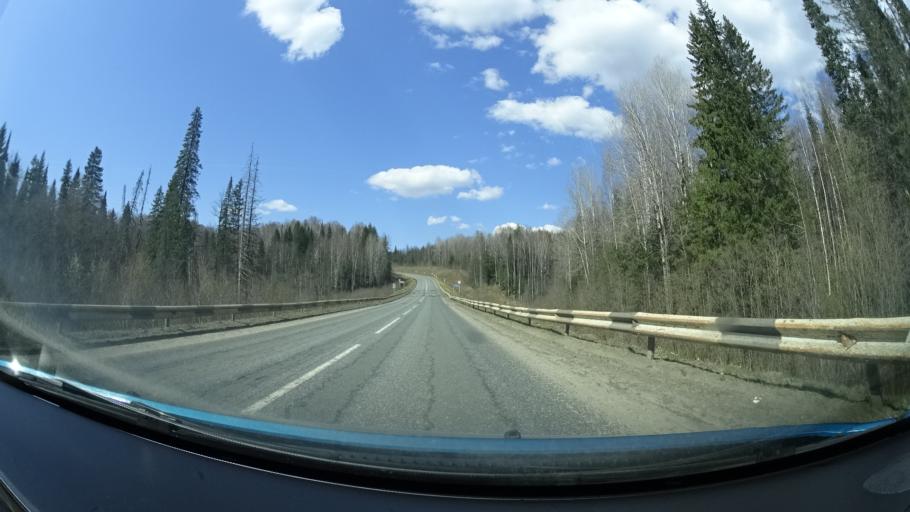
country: RU
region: Perm
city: Yugo-Kamskiy
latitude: 57.5921
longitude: 55.6654
